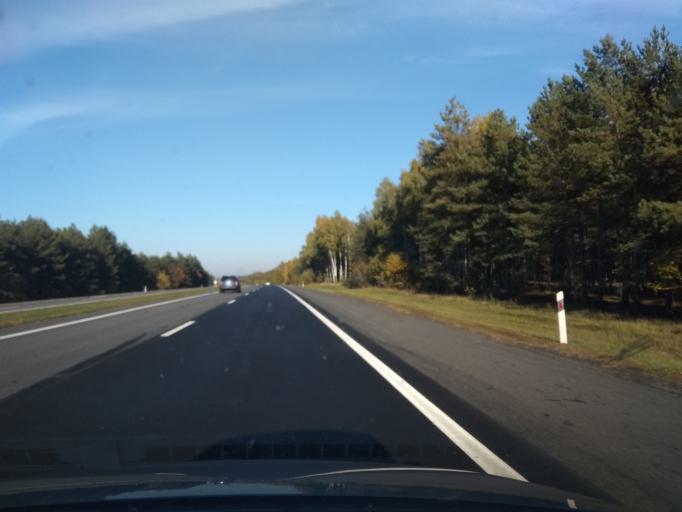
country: BY
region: Brest
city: Nyakhachava
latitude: 52.5854
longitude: 25.1336
